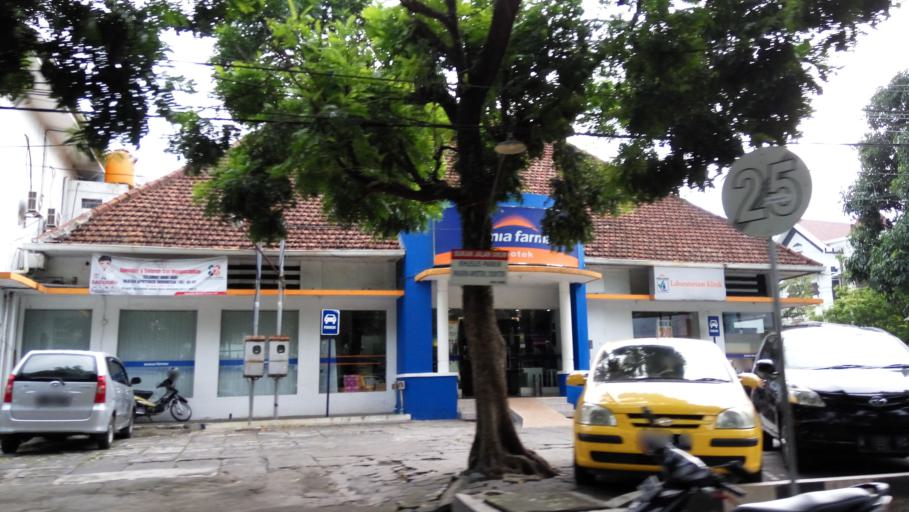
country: ID
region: East Java
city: Malang
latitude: -7.9791
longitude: 112.6246
